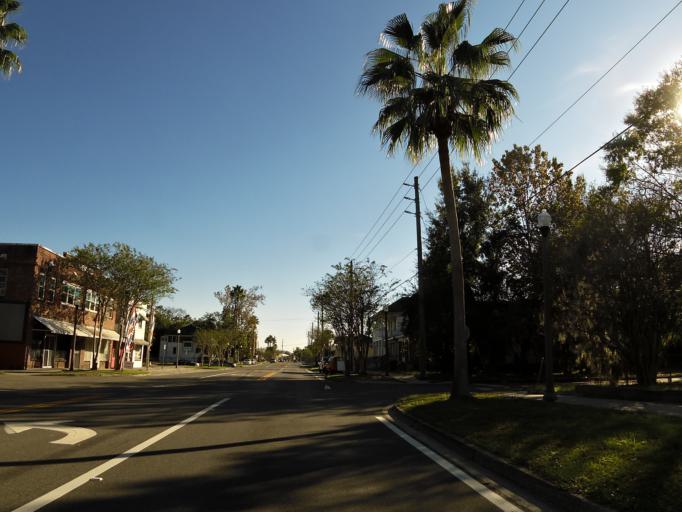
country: US
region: Florida
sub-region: Duval County
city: Jacksonville
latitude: 30.3437
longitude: -81.6756
